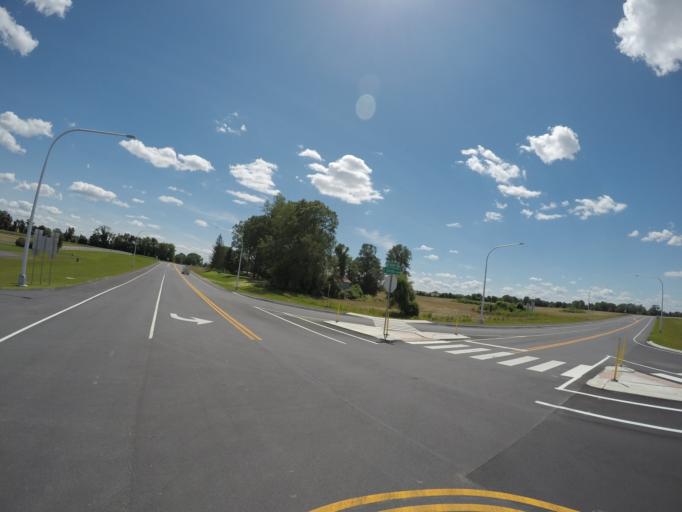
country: US
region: Delaware
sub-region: Sussex County
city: Milford
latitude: 38.9246
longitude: -75.4147
